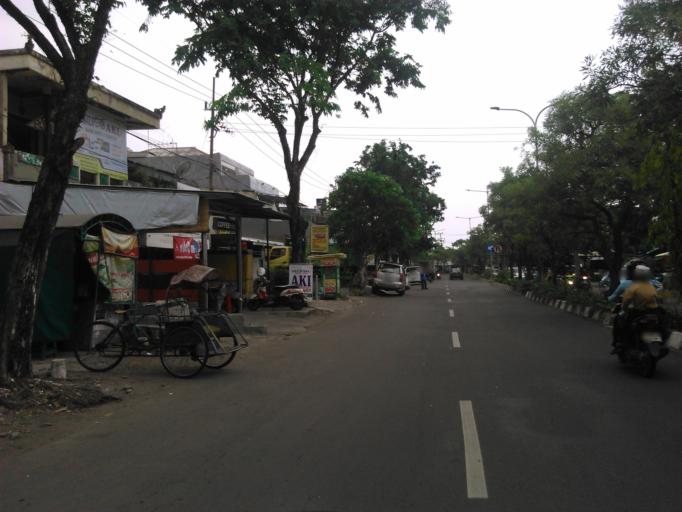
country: ID
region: East Java
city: Gubengairlangga
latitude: -7.2756
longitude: 112.7624
